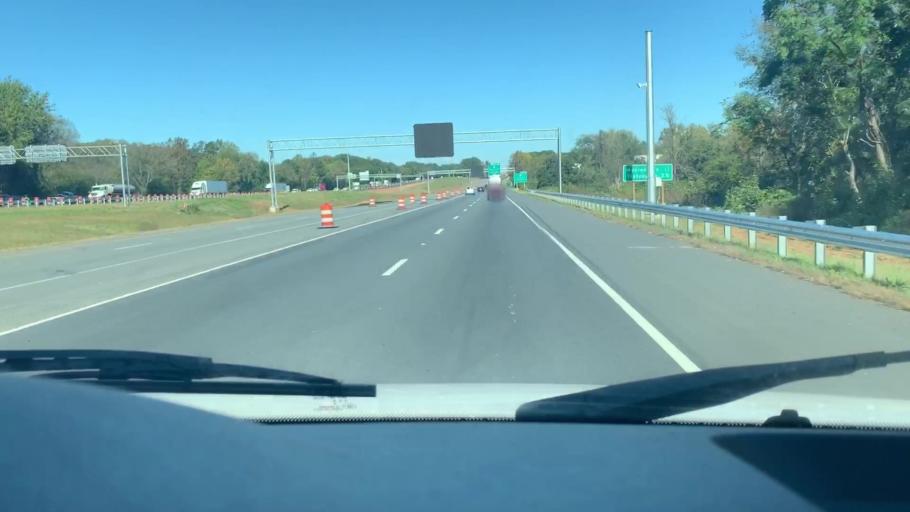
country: US
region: North Carolina
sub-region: Mecklenburg County
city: Huntersville
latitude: 35.4235
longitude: -80.8629
